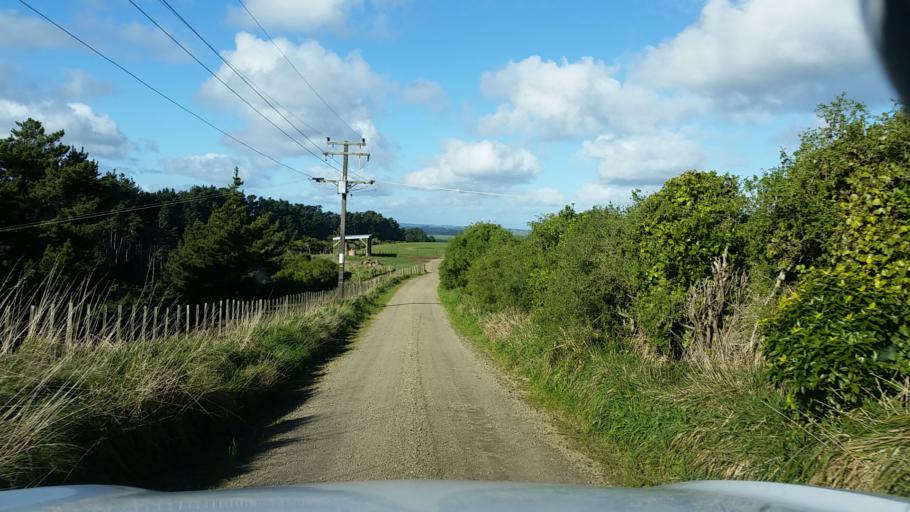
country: NZ
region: Taranaki
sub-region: South Taranaki District
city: Patea
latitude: -39.6882
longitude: 174.5512
